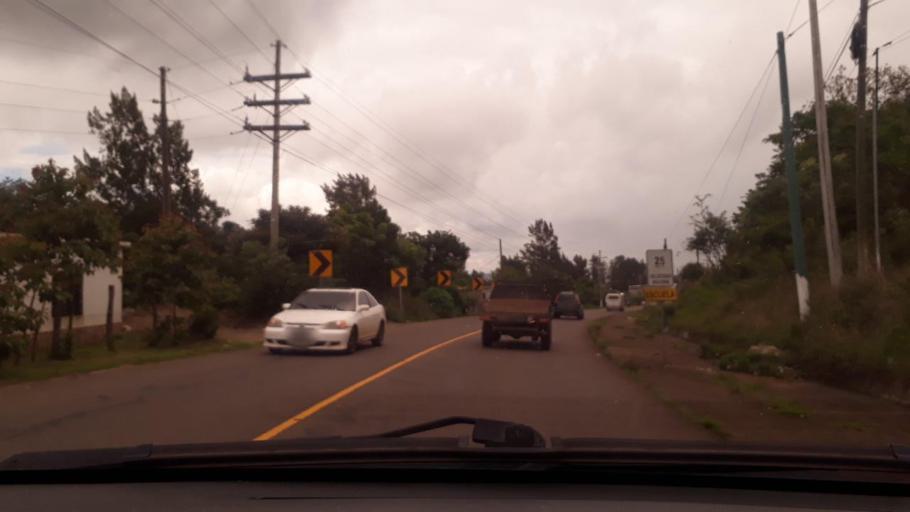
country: GT
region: Jutiapa
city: Conguaco
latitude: 14.0547
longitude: -90.0520
